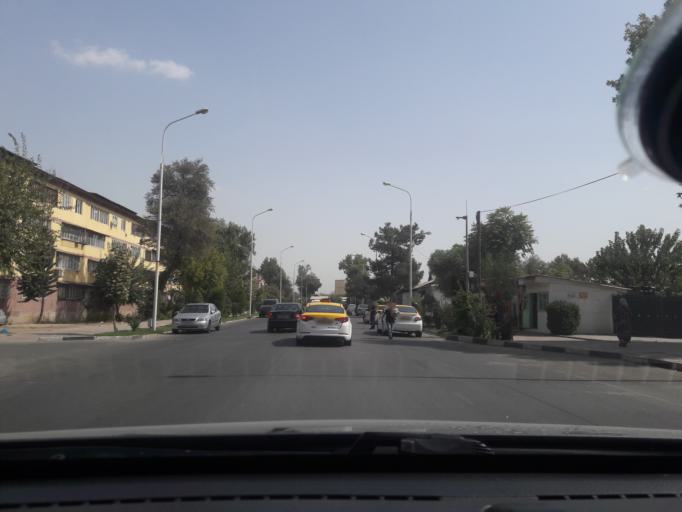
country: TJ
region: Dushanbe
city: Dushanbe
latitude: 38.5641
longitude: 68.7596
